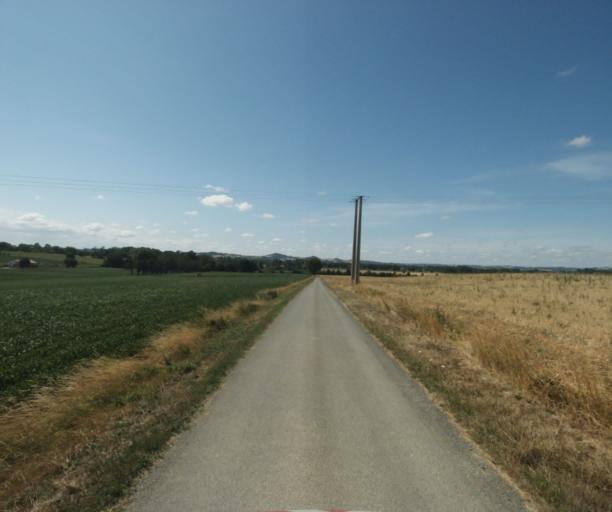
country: FR
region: Midi-Pyrenees
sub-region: Departement de la Haute-Garonne
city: Revel
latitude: 43.4853
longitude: 2.0020
